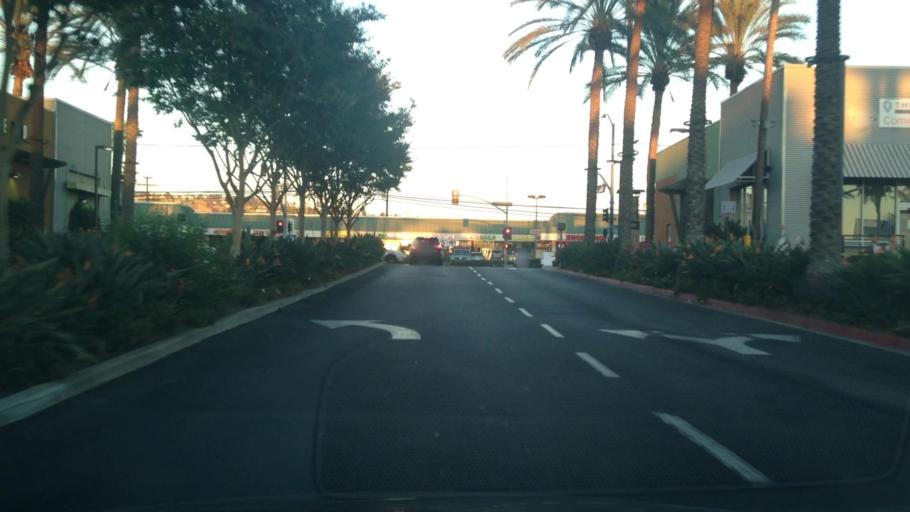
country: US
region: California
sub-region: Orange County
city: Villa Park
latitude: 33.8261
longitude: -117.8369
